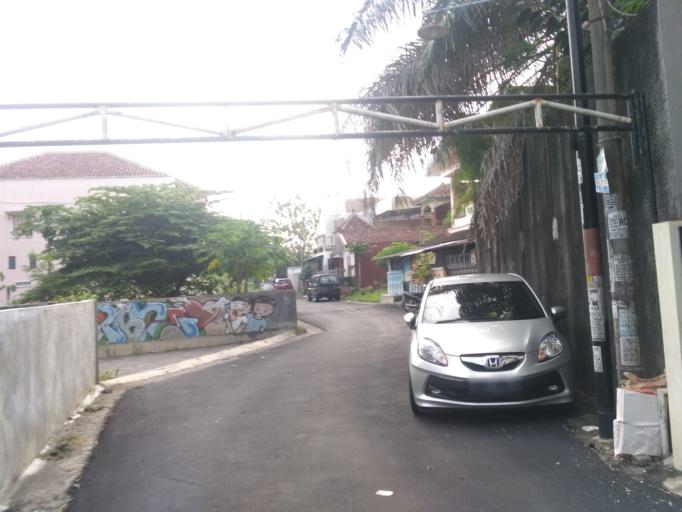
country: ID
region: Daerah Istimewa Yogyakarta
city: Depok
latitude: -7.7676
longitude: 110.4093
